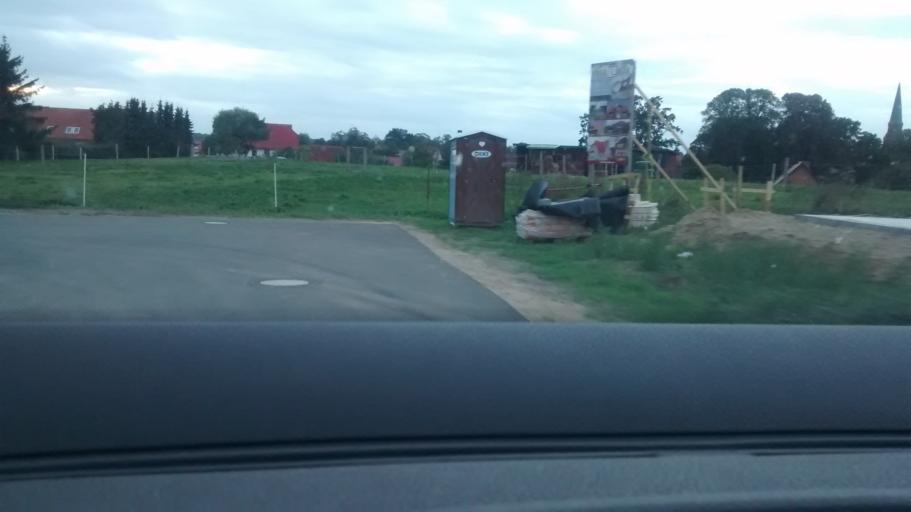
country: DE
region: Mecklenburg-Vorpommern
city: Lubtheen
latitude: 53.3993
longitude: 10.9719
